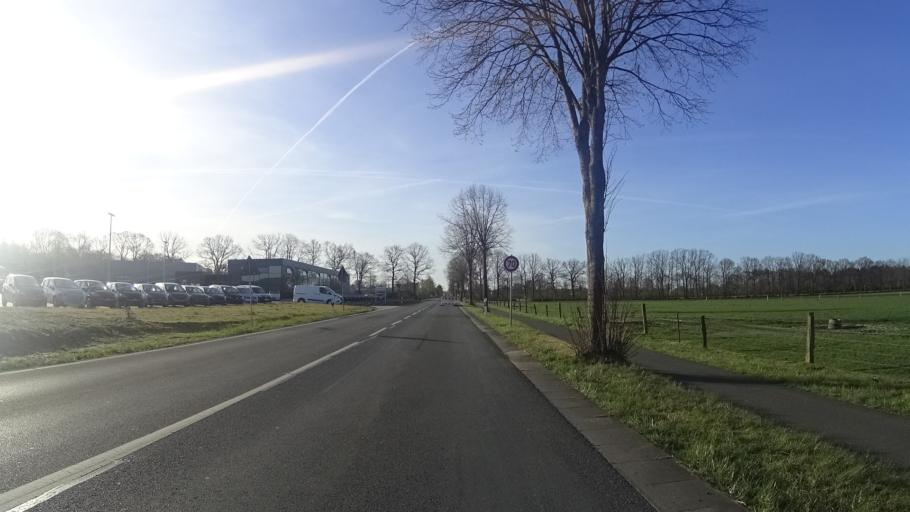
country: DE
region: North Rhine-Westphalia
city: Emsdetten
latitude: 52.1401
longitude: 7.5394
